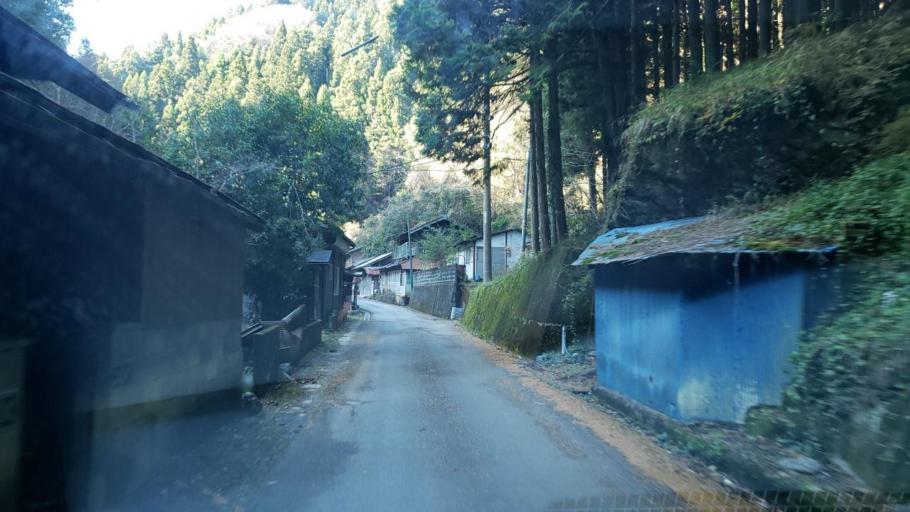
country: JP
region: Tokushima
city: Wakimachi
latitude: 33.9894
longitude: 133.9920
